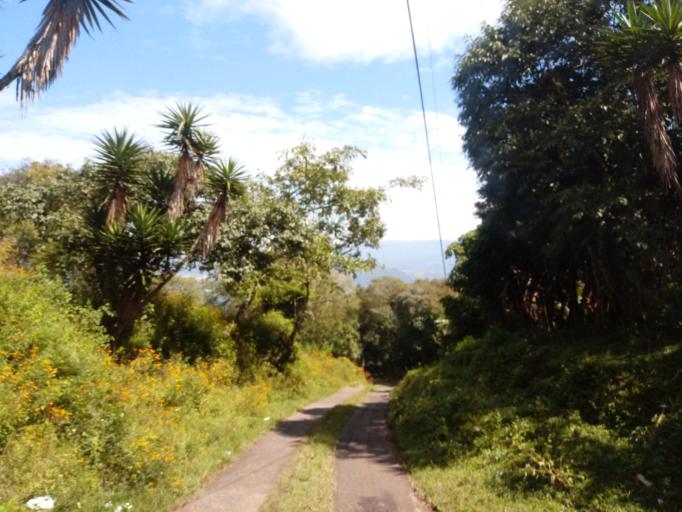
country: GT
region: Guatemala
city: Amatitlan
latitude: 14.4608
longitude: -90.6067
